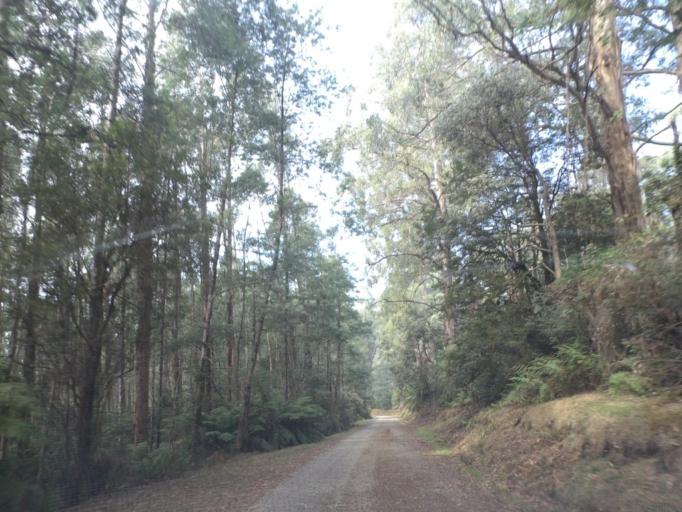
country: AU
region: Victoria
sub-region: Yarra Ranges
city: Healesville
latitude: -37.5664
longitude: 145.5411
